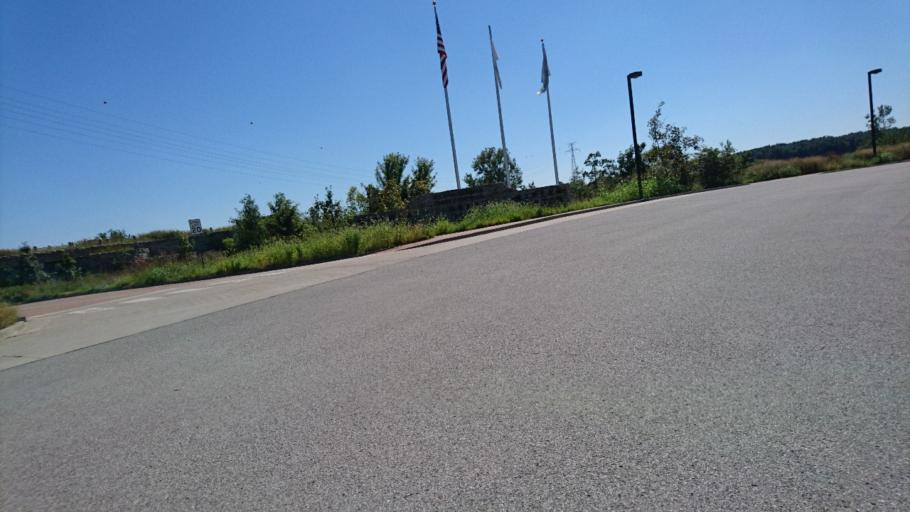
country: US
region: Illinois
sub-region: Madison County
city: East Alton
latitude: 38.8675
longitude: -90.1414
